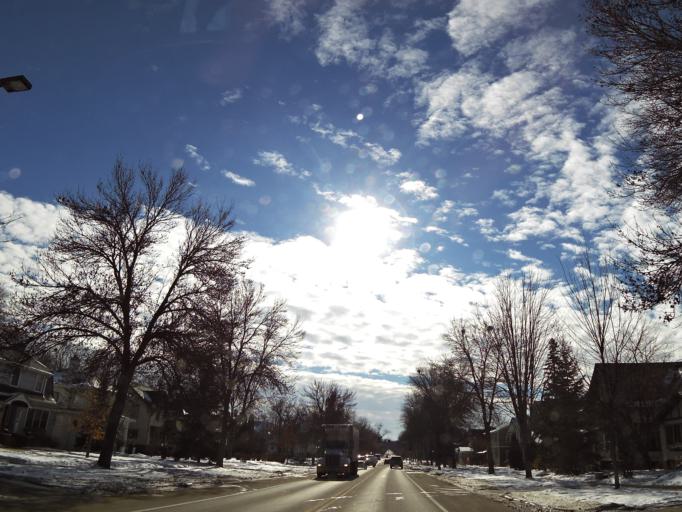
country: US
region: Minnesota
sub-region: Hennepin County
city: Richfield
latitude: 44.9263
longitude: -93.2883
